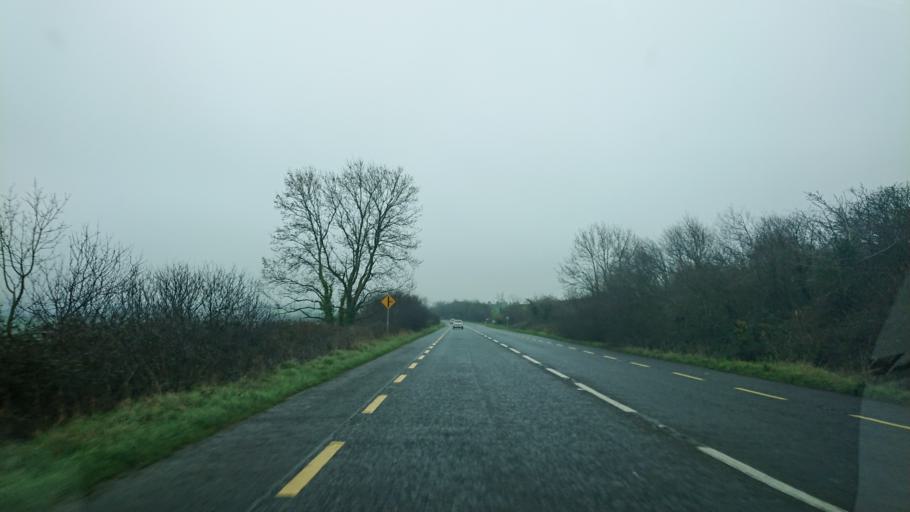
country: IE
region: Munster
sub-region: County Cork
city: Killumney
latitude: 51.7860
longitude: -8.6249
